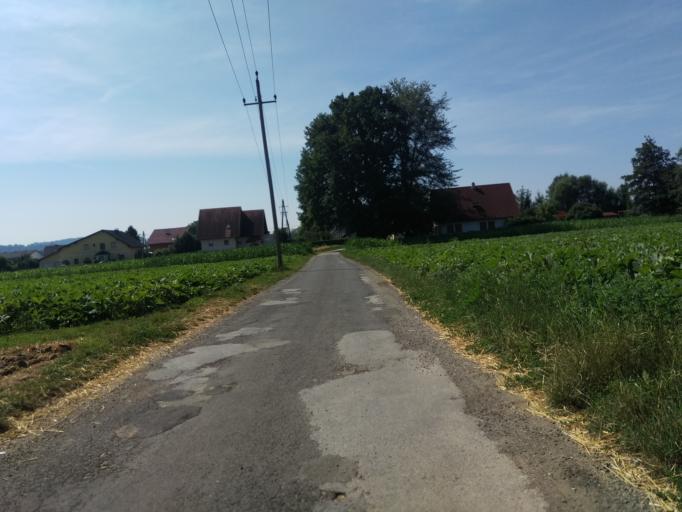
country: AT
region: Styria
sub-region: Politischer Bezirk Graz-Umgebung
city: Gossendorf
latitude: 46.9876
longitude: 15.4884
